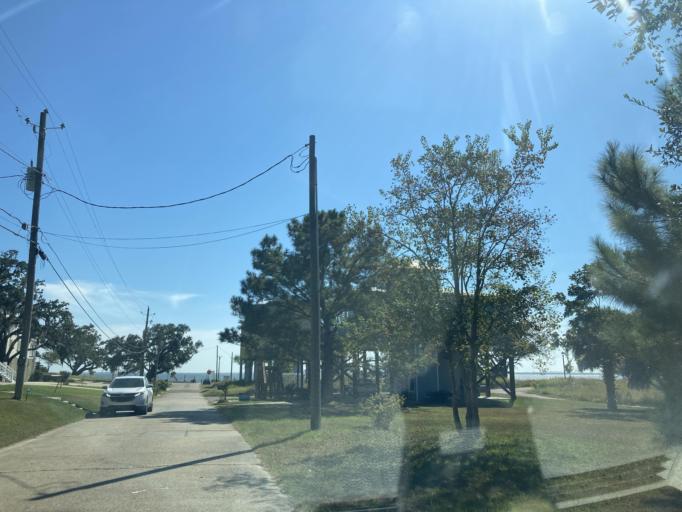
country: US
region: Mississippi
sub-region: Jackson County
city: Ocean Springs
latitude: 30.4088
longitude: -88.8333
